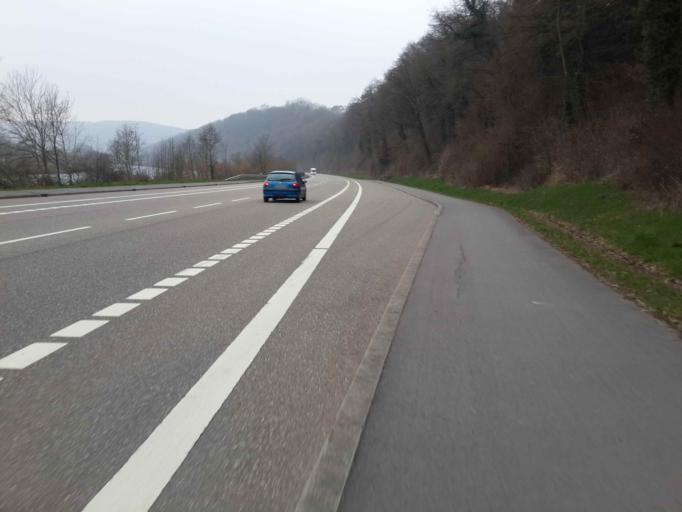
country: DE
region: Baden-Wuerttemberg
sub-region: Karlsruhe Region
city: Obrigheim
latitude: 49.3692
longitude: 9.0836
